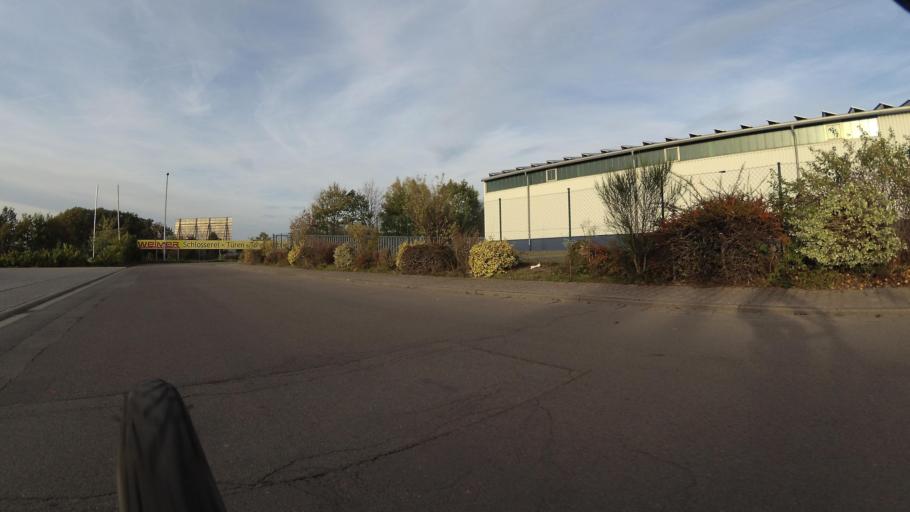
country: DE
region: Rheinland-Pfalz
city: Steinwenden
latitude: 49.4369
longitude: 7.5354
